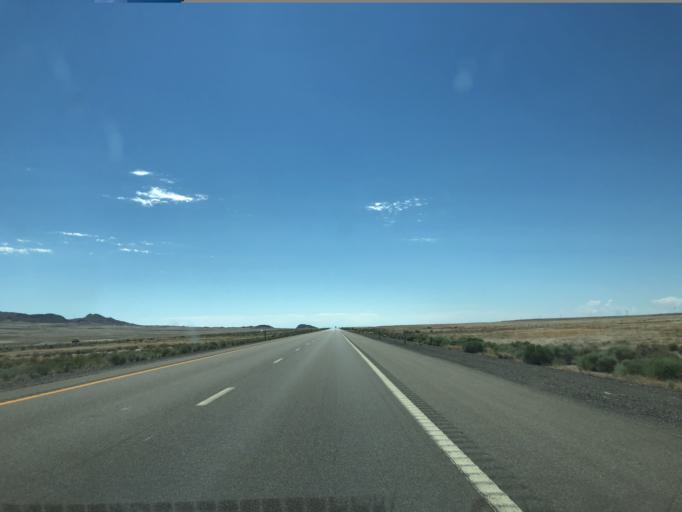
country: US
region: Nevada
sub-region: Elko County
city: West Wendover
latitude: 40.8057
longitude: -114.1733
